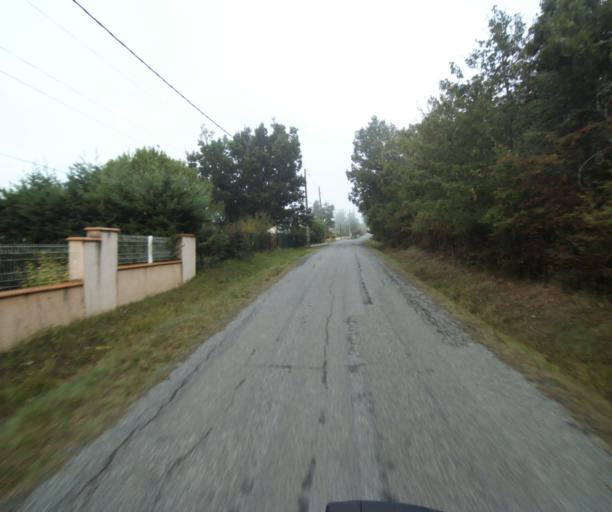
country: FR
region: Midi-Pyrenees
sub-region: Departement du Tarn-et-Garonne
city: Orgueil
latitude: 43.9309
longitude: 1.4220
